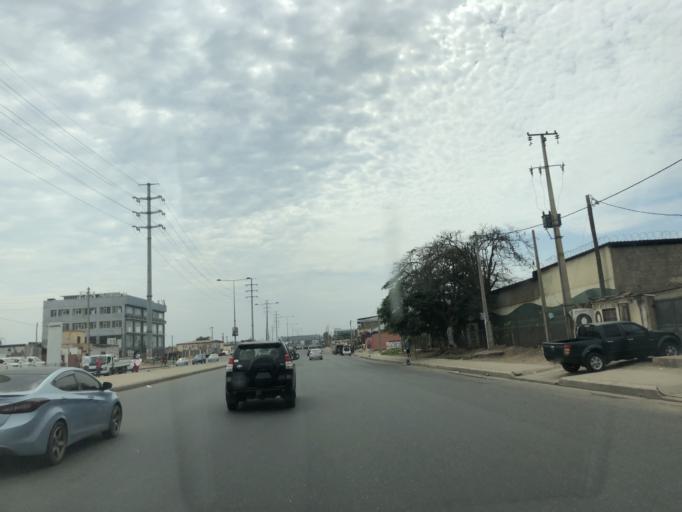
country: AO
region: Luanda
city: Luanda
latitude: -8.8443
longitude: 13.2763
